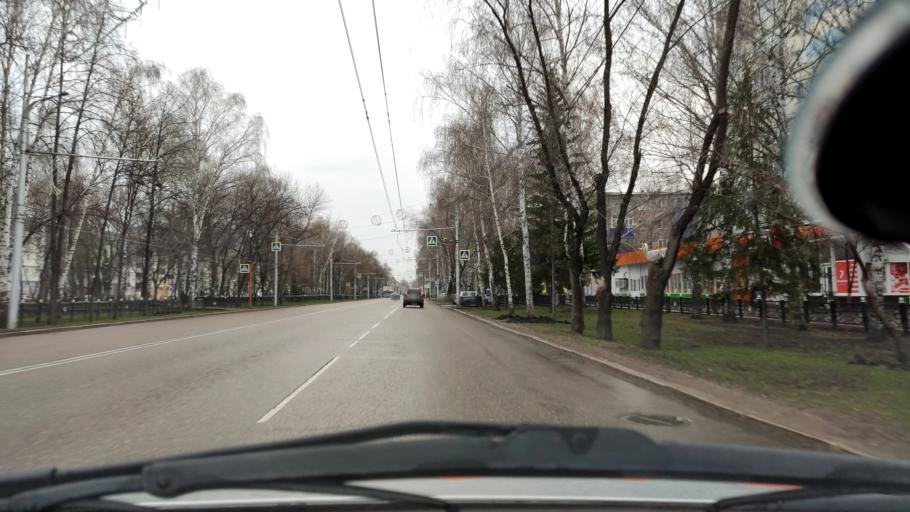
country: RU
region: Bashkortostan
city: Sterlitamak
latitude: 53.6334
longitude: 55.9337
